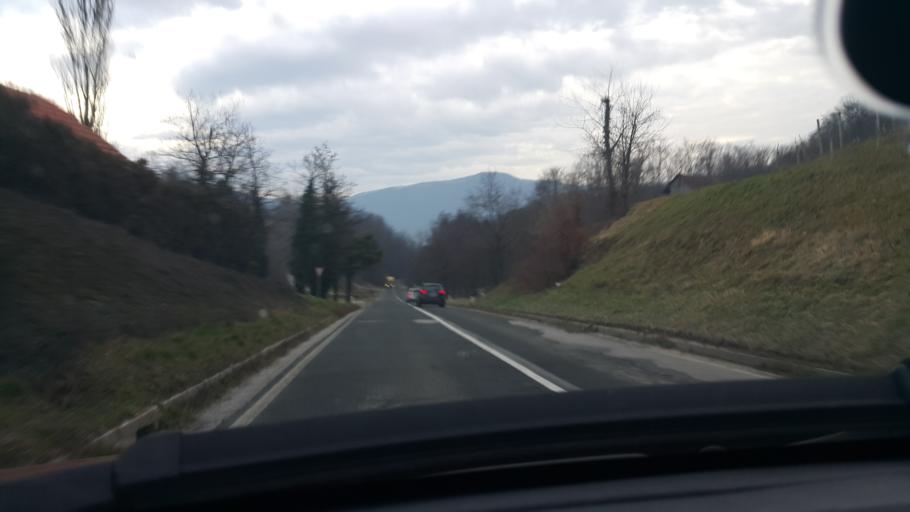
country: SI
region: Bistrica ob Sotli
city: Bistrica ob Sotli
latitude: 46.0751
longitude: 15.6401
